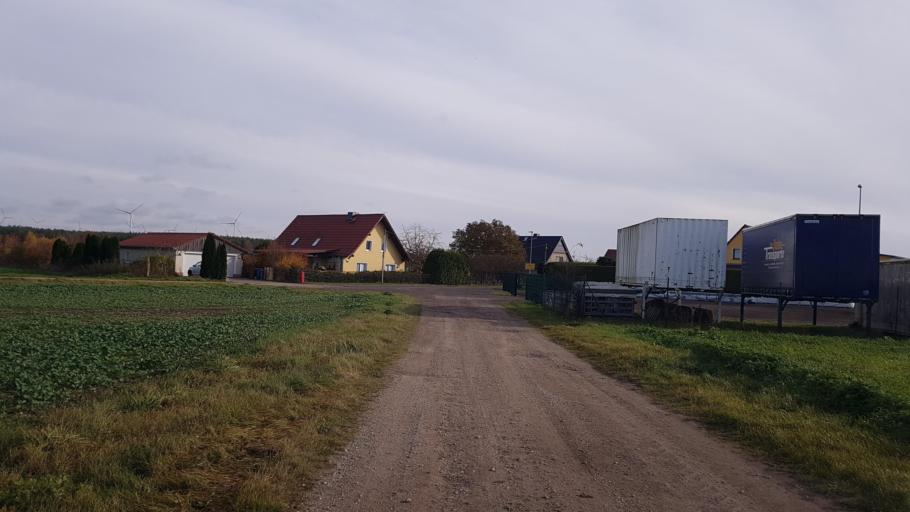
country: DE
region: Brandenburg
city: Niedergorsdorf
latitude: 52.0151
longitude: 12.9166
